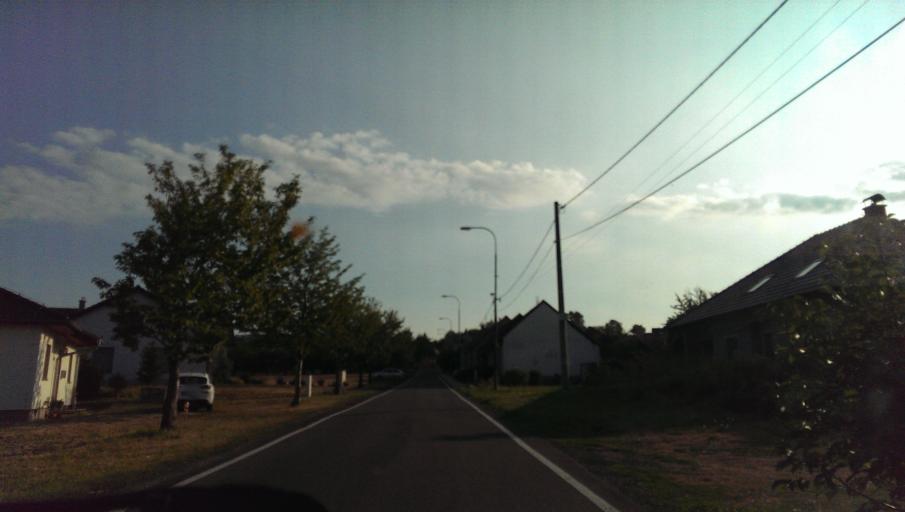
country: CZ
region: South Moravian
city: Zeravice
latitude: 49.0620
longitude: 17.2207
